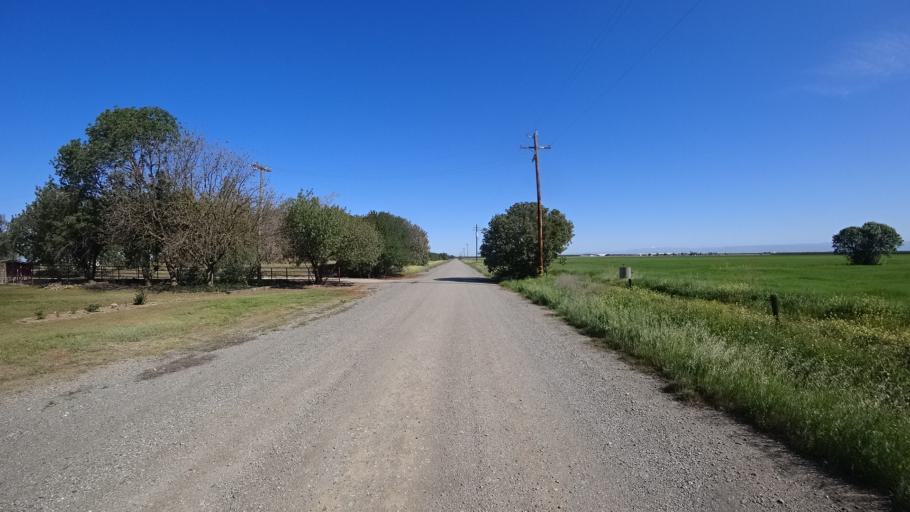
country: US
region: California
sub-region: Glenn County
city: Orland
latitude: 39.6454
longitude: -122.1598
